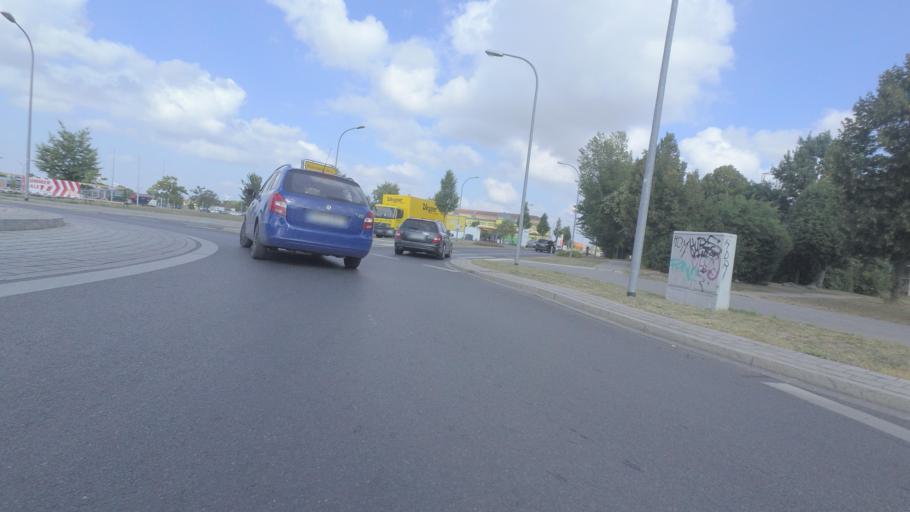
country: DE
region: Brandenburg
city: Neuruppin
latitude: 52.9174
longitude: 12.7908
